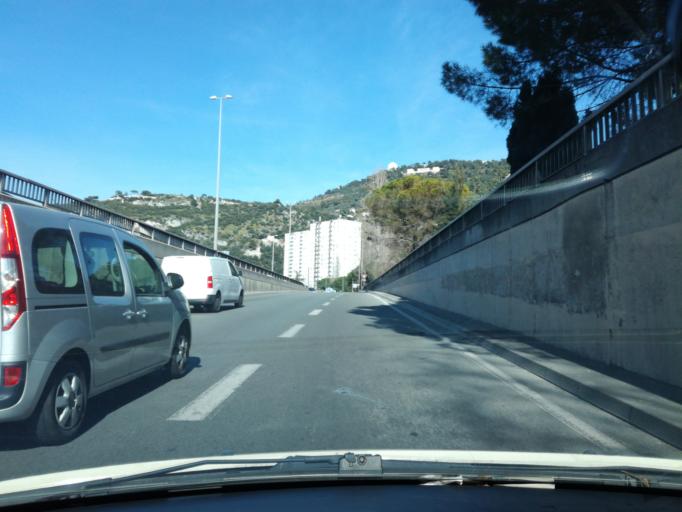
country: FR
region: Provence-Alpes-Cote d'Azur
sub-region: Departement des Alpes-Maritimes
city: Saint-Andre-de-la-Roche
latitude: 43.7193
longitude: 7.2854
